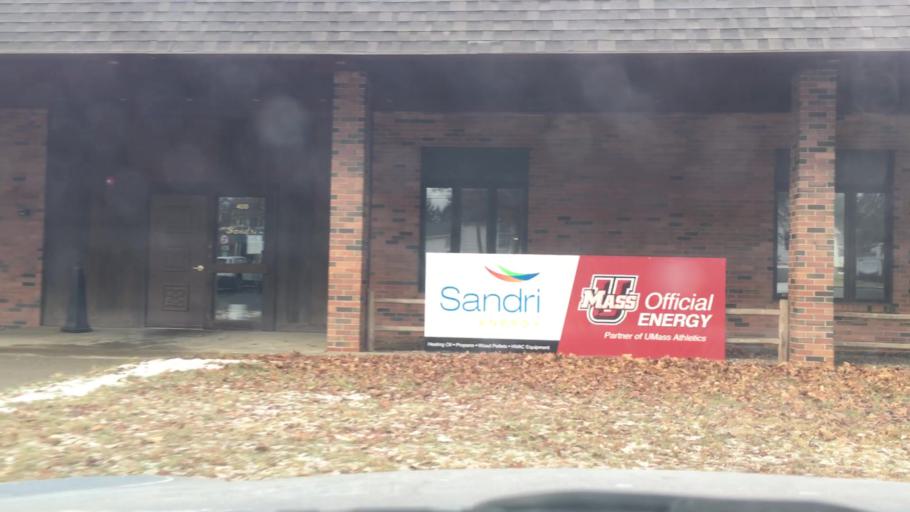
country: US
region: Massachusetts
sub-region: Franklin County
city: Greenfield
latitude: 42.6050
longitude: -72.6037
